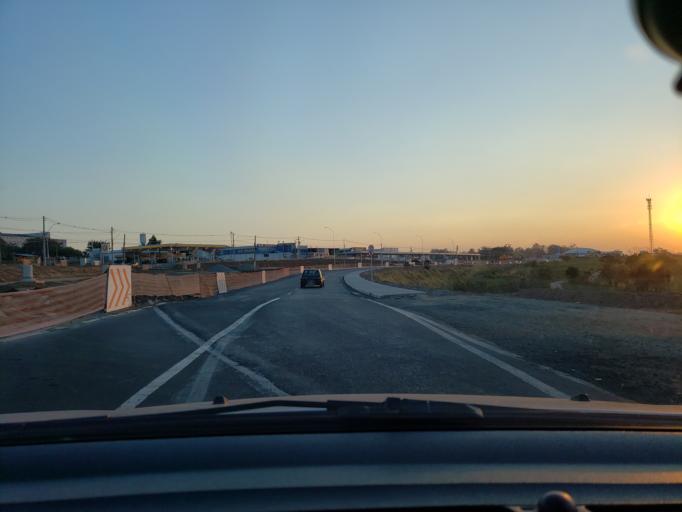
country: BR
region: Sao Paulo
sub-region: Campinas
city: Campinas
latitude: -22.9418
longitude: -47.1433
